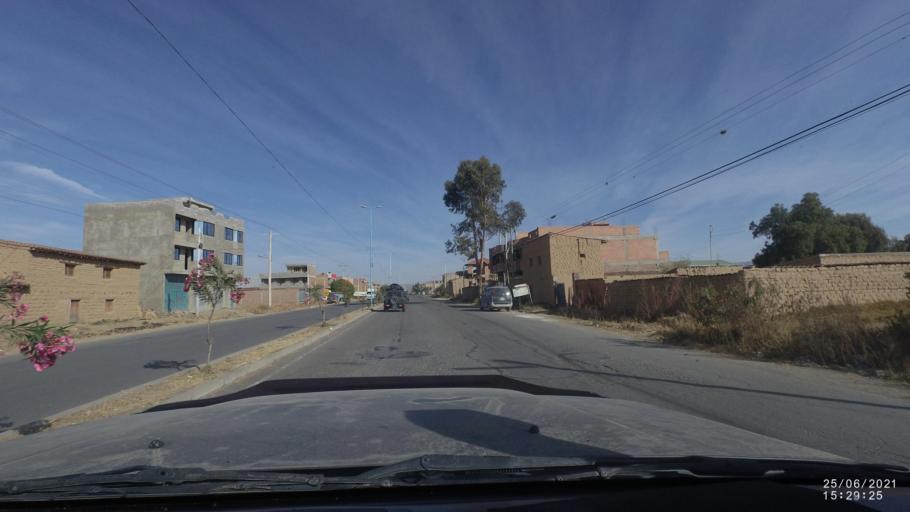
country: BO
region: Cochabamba
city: Cliza
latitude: -17.5721
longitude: -65.9350
